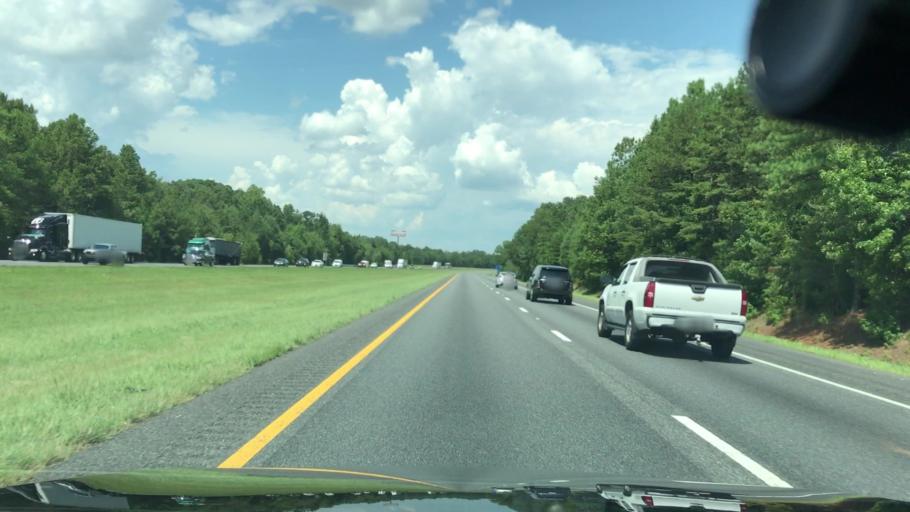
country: US
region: South Carolina
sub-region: York County
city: Lesslie
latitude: 34.8779
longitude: -81.0010
